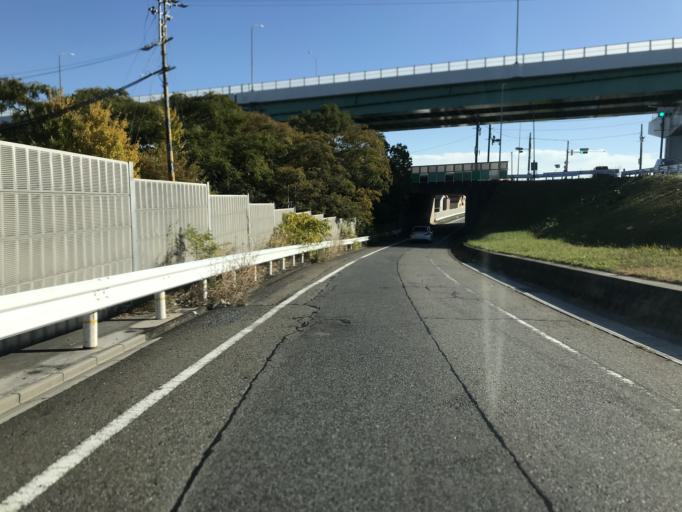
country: JP
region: Aichi
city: Kanie
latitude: 35.1583
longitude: 136.8391
